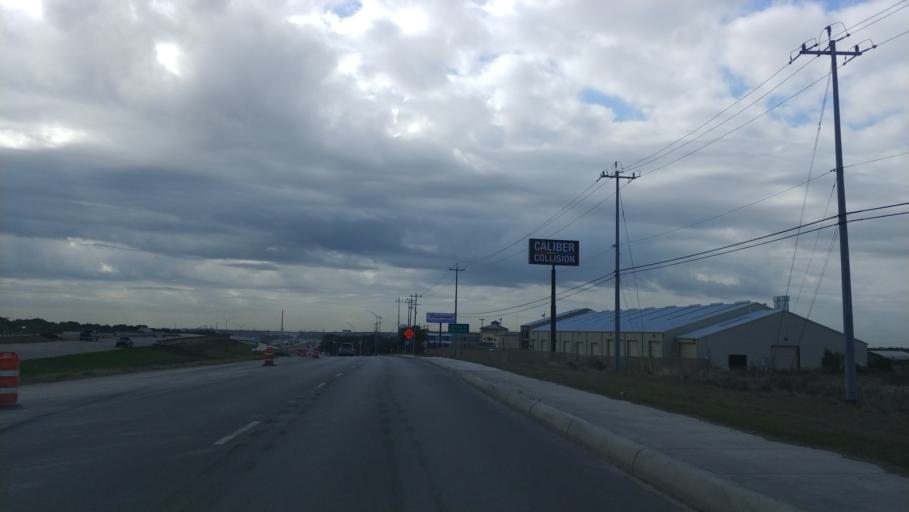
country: US
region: Texas
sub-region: Bexar County
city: Leon Valley
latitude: 29.4508
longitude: -98.7120
